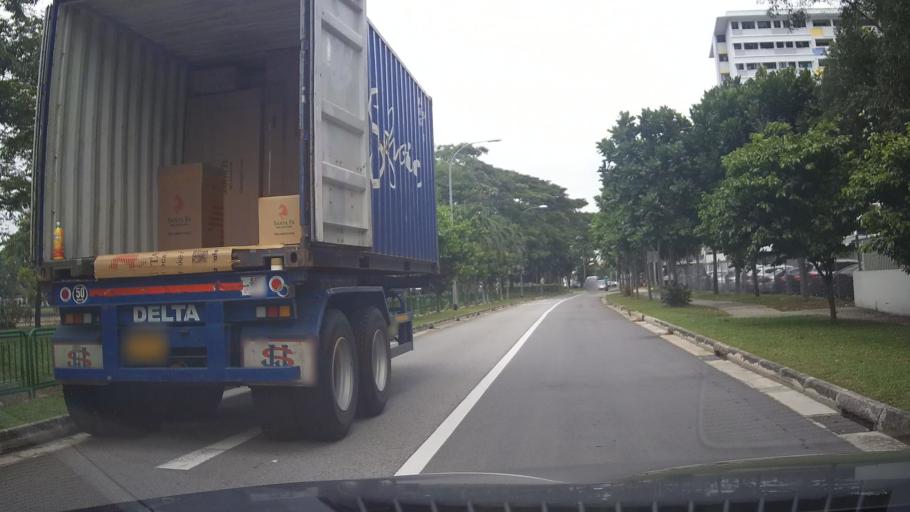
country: SG
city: Singapore
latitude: 1.3014
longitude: 103.8814
